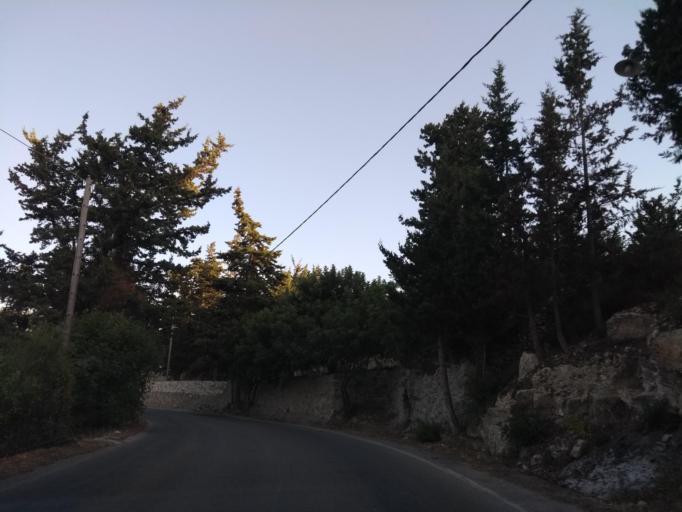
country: GR
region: Crete
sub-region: Nomos Chanias
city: Kalivai
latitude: 35.4326
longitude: 24.1796
